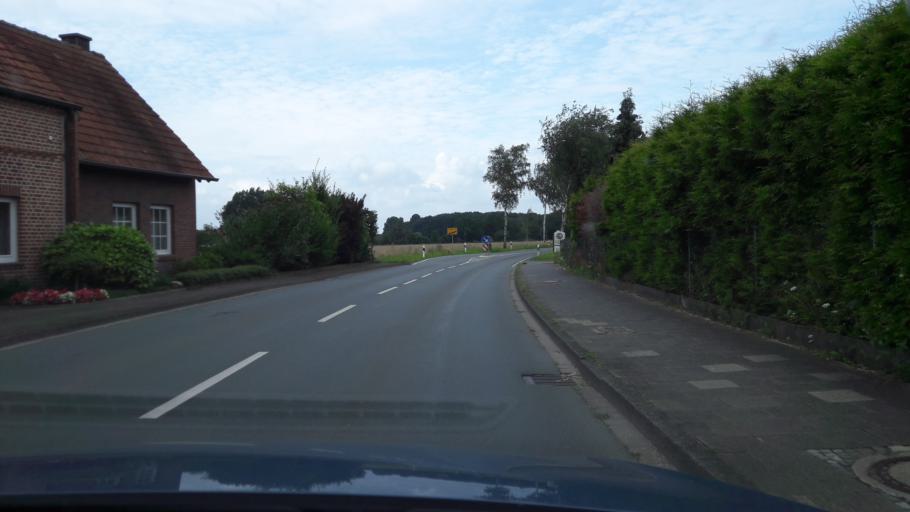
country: DE
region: North Rhine-Westphalia
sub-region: Regierungsbezirk Munster
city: Everswinkel
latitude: 51.8749
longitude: 7.9042
